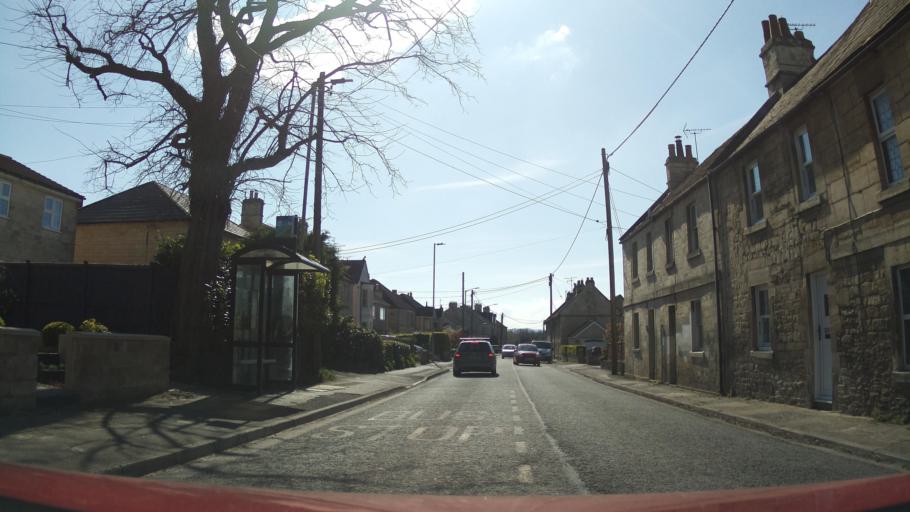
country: GB
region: England
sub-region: Wiltshire
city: Bradford-on-Avon
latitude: 51.3392
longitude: -2.2425
